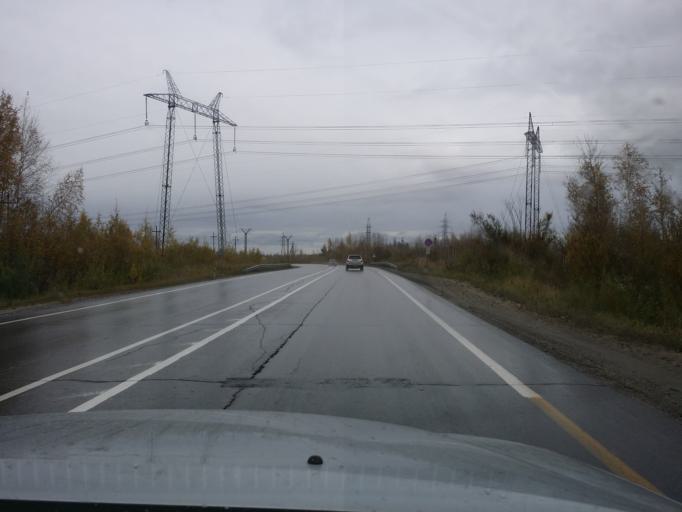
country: RU
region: Khanty-Mansiyskiy Avtonomnyy Okrug
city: Megion
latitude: 61.0809
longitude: 76.1176
